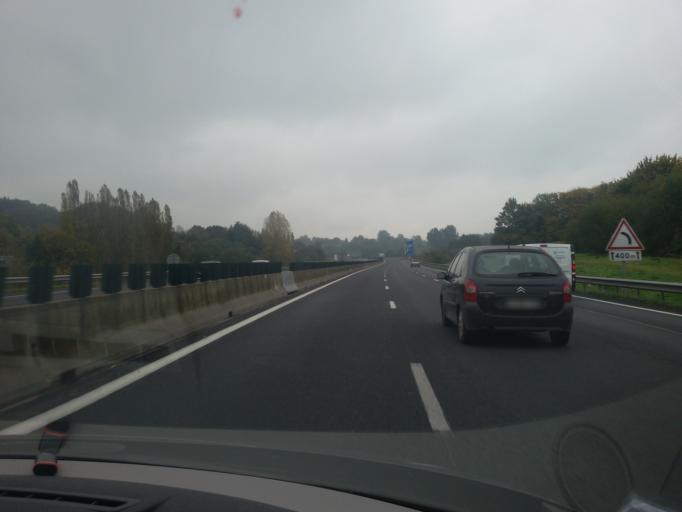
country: FR
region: Haute-Normandie
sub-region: Departement de l'Eure
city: Beuzeville
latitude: 49.3030
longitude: 0.2846
